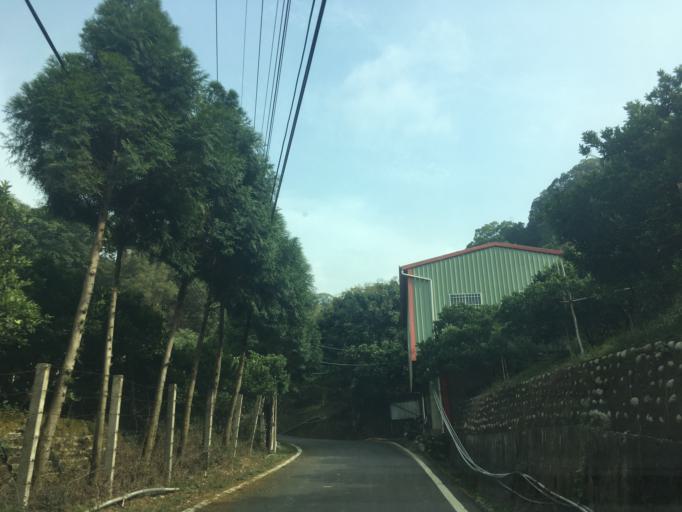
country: TW
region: Taiwan
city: Fengyuan
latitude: 24.2202
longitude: 120.7625
